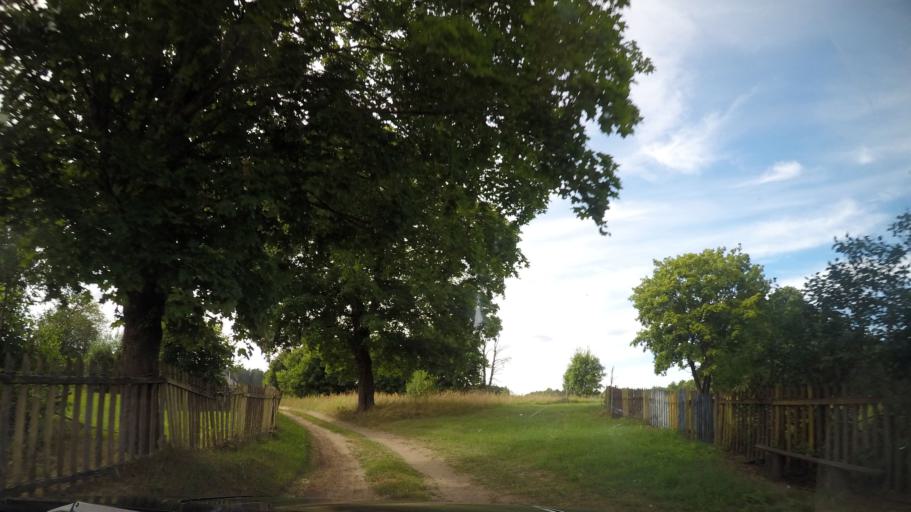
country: BY
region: Grodnenskaya
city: Skidal'
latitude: 53.8386
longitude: 24.1891
